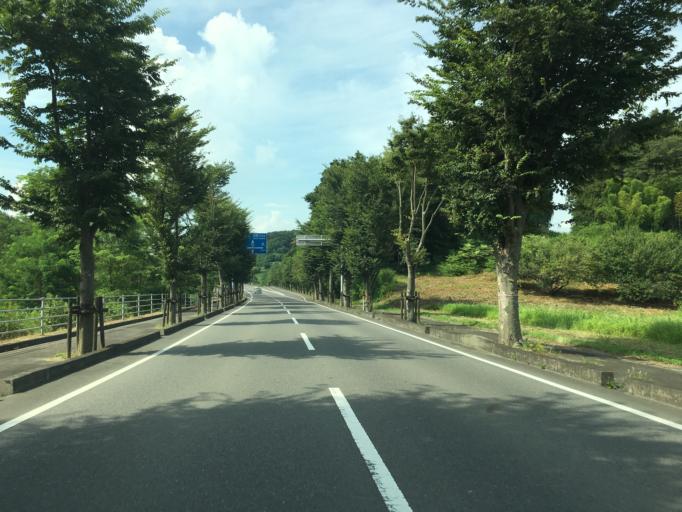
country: JP
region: Fukushima
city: Sukagawa
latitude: 37.2397
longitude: 140.4352
